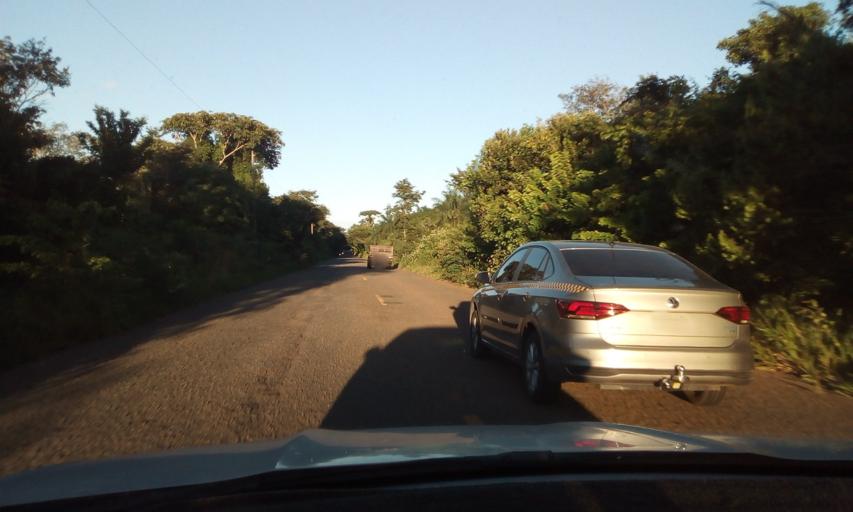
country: BR
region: Paraiba
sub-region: Areia
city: Remigio
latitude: -6.9648
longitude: -35.7458
